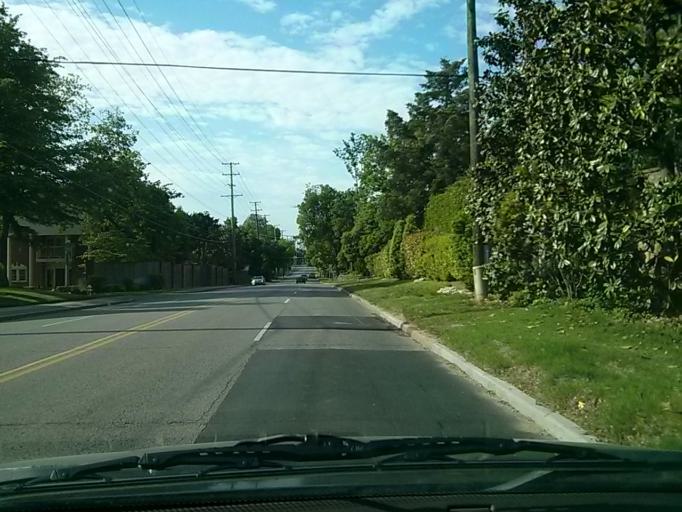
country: US
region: Oklahoma
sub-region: Tulsa County
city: Tulsa
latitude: 36.1279
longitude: -95.9757
